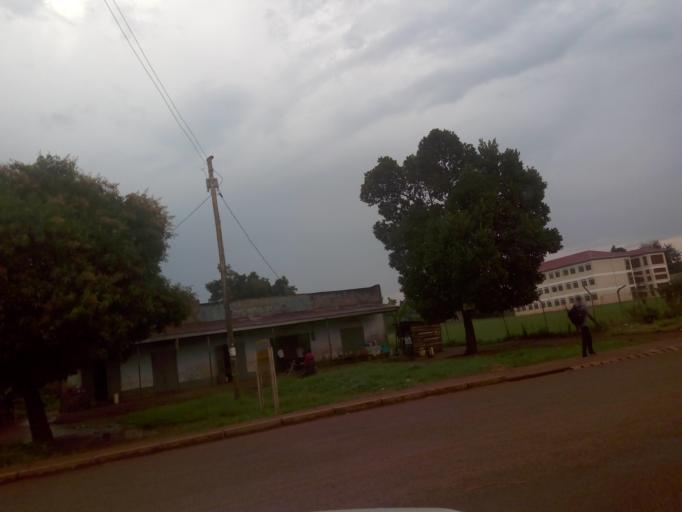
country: UG
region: Western Region
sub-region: Masindi District
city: Masindi
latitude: 1.6897
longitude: 31.7072
